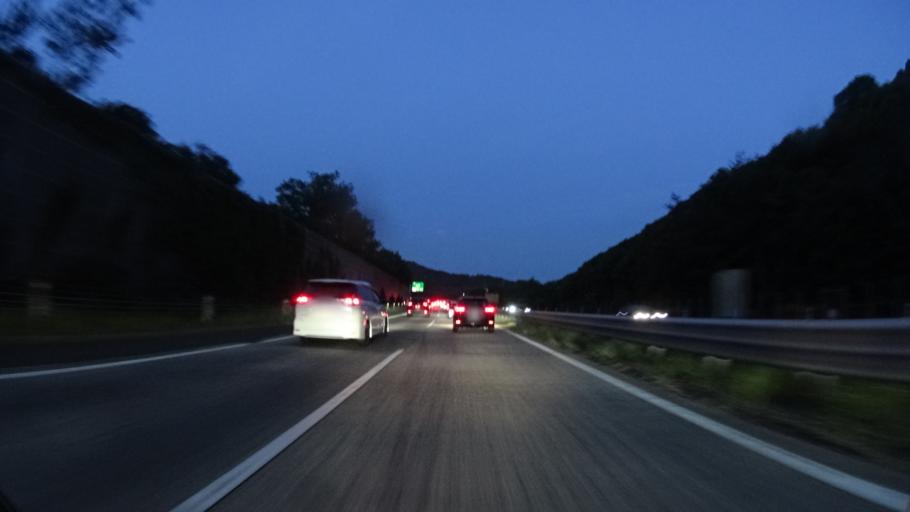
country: JP
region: Hyogo
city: Kariya
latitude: 34.7742
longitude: 134.3613
